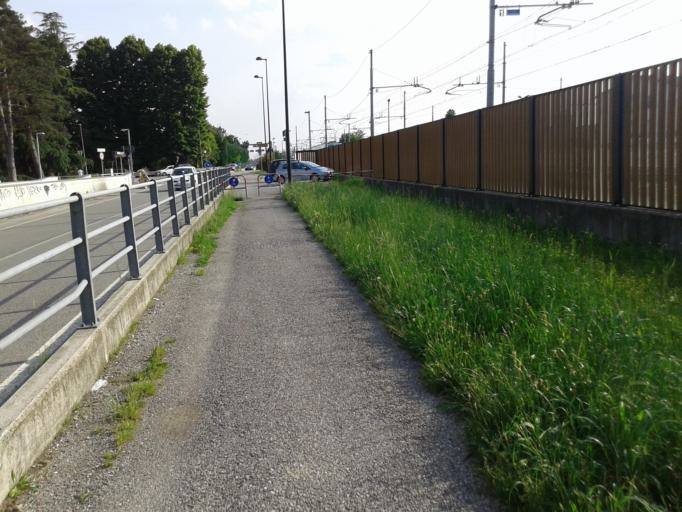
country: IT
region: Veneto
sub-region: Provincia di Padova
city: Camposampiero
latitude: 45.5742
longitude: 11.9307
